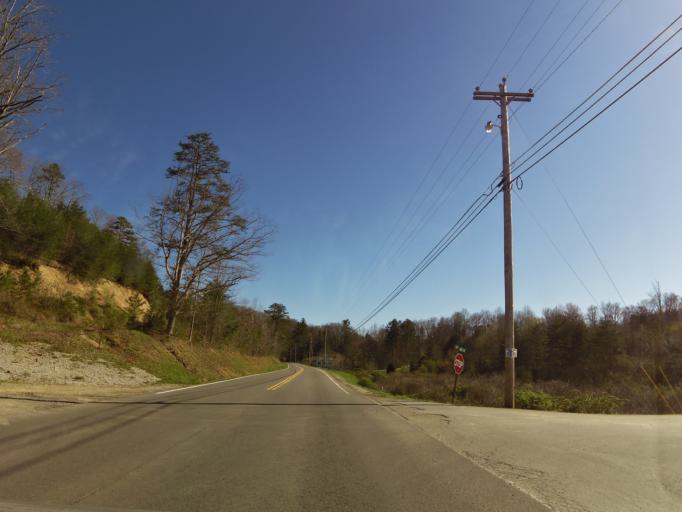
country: US
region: Tennessee
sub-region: Scott County
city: Oneida
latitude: 36.4848
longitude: -84.5075
